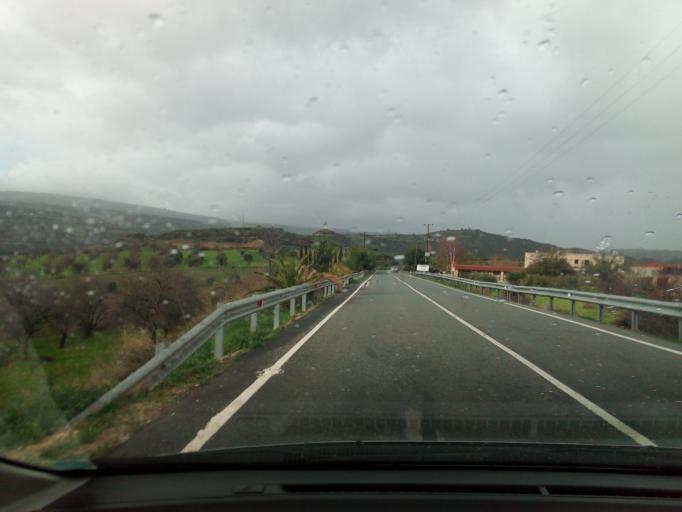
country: CY
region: Pafos
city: Polis
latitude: 34.9568
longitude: 32.4801
